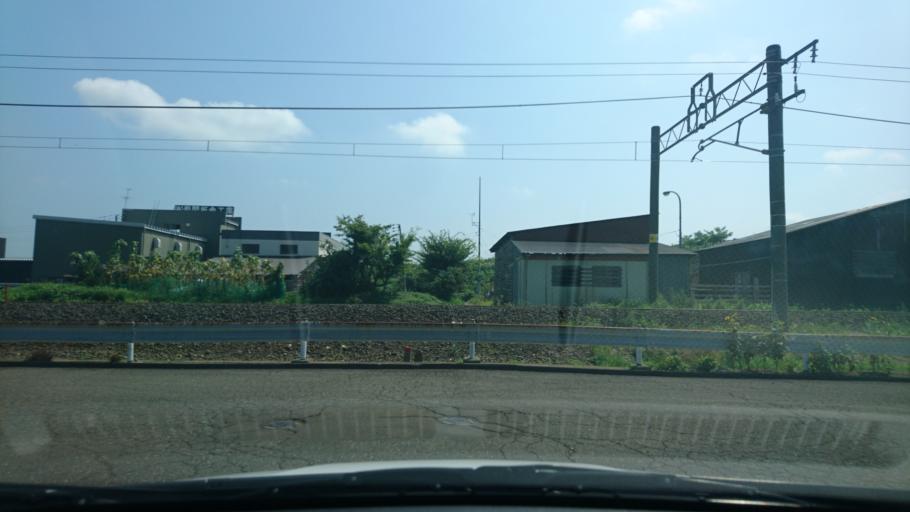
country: JP
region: Niigata
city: Arai
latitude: 37.0589
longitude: 138.2568
